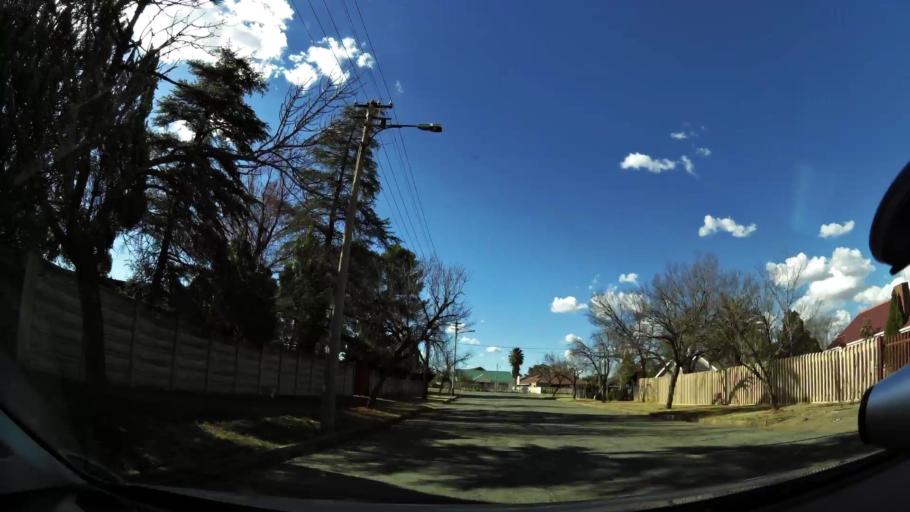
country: ZA
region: North-West
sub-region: Dr Kenneth Kaunda District Municipality
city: Klerksdorp
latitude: -26.8434
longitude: 26.6547
